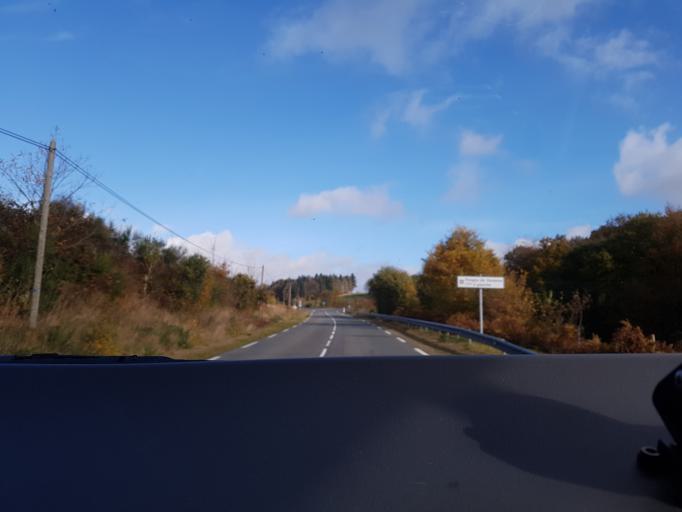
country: FR
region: Lower Normandy
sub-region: Departement de l'Orne
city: Champsecret
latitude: 48.6204
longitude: -0.5775
